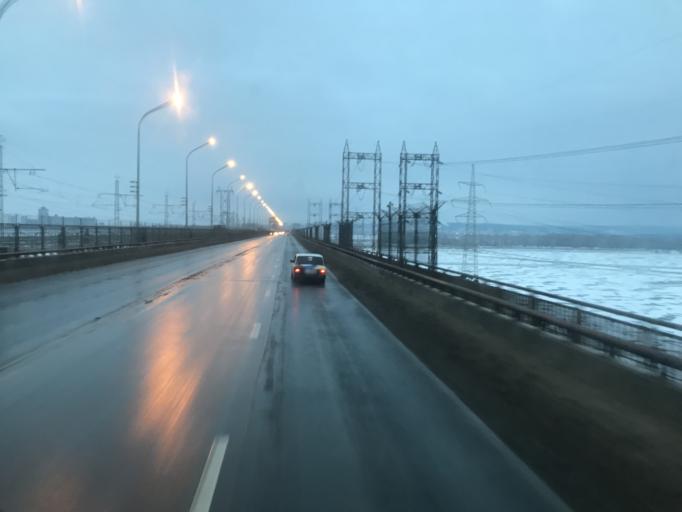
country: RU
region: Samara
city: Zhigulevsk
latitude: 53.4537
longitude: 49.4928
